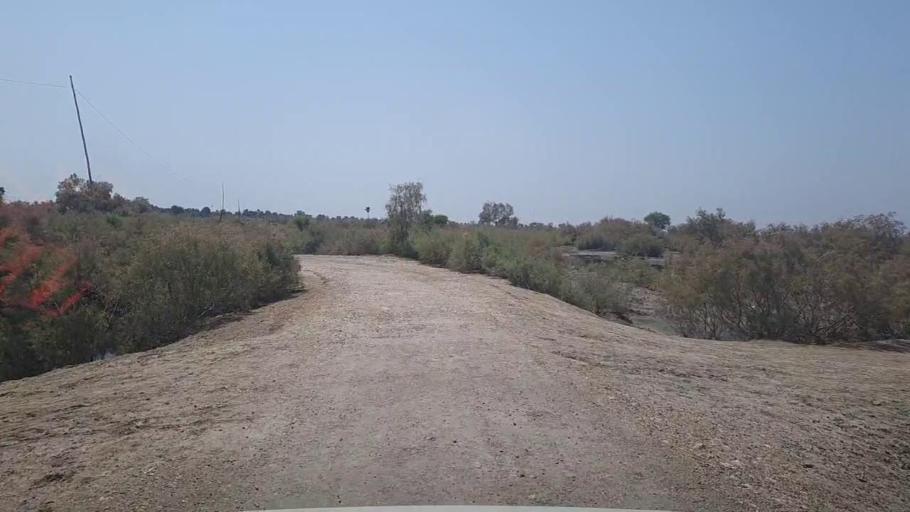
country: PK
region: Sindh
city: Kandhkot
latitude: 28.3091
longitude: 69.3569
